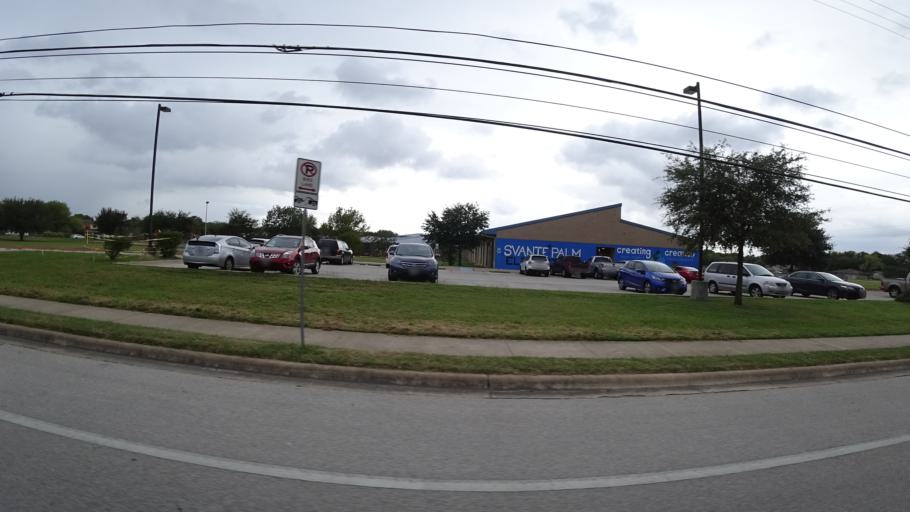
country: US
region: Texas
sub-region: Travis County
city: Onion Creek
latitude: 30.1644
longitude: -97.7423
